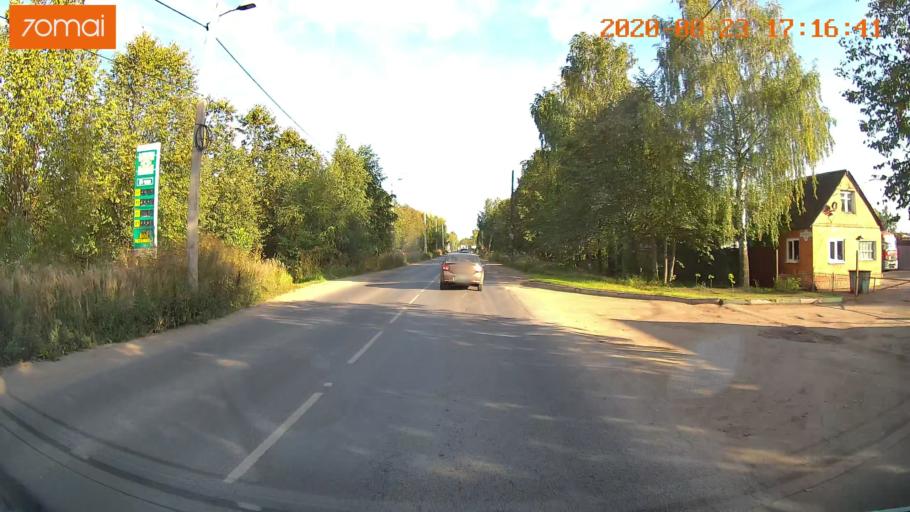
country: RU
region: Ivanovo
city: Novo-Talitsy
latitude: 57.0373
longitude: 40.9126
